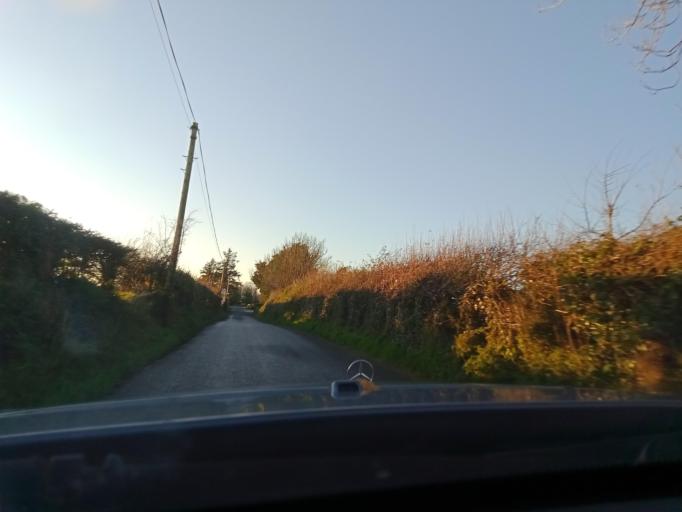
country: IE
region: Munster
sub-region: Waterford
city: Waterford
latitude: 52.3734
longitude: -7.1376
